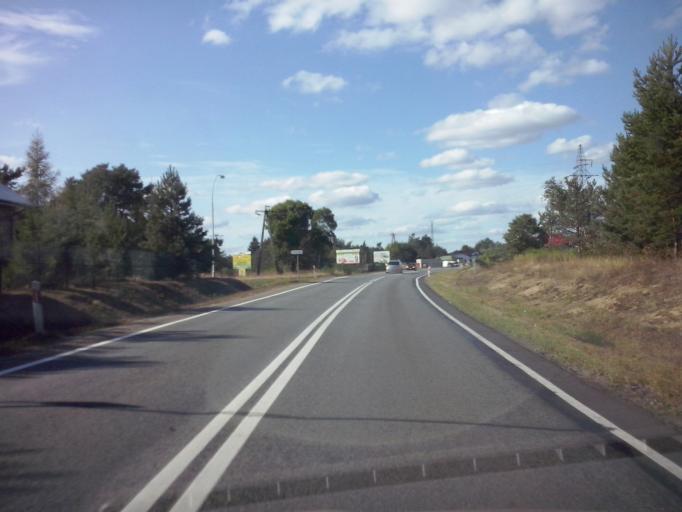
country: PL
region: Subcarpathian Voivodeship
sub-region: Powiat nizanski
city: Rudnik nad Sanem
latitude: 50.4535
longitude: 22.2438
